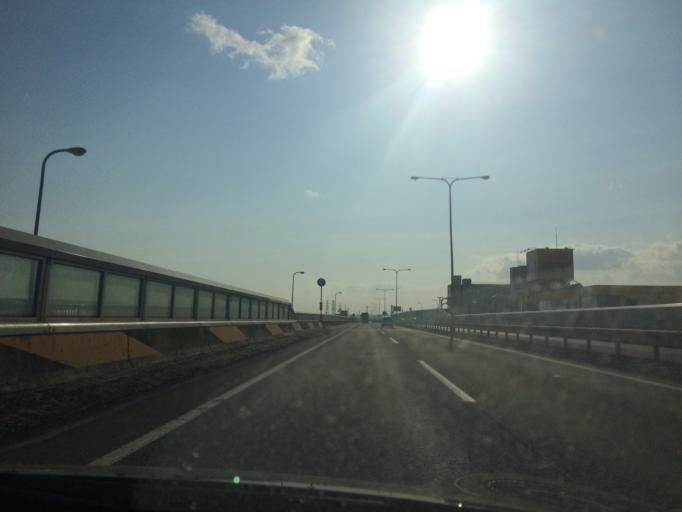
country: JP
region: Hokkaido
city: Sapporo
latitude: 43.0977
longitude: 141.3928
